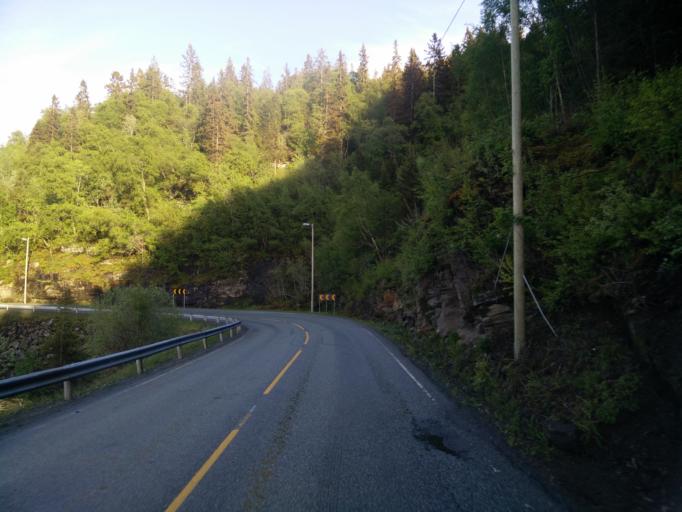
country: NO
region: Sor-Trondelag
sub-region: Skaun
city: Borsa
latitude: 63.3281
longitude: 10.1032
